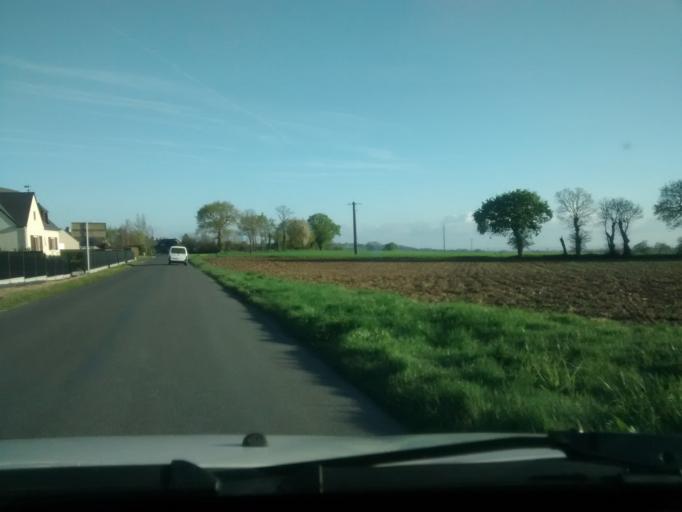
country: FR
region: Brittany
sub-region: Departement d'Ille-et-Vilaine
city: Pleine-Fougeres
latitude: 48.5376
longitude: -1.5675
